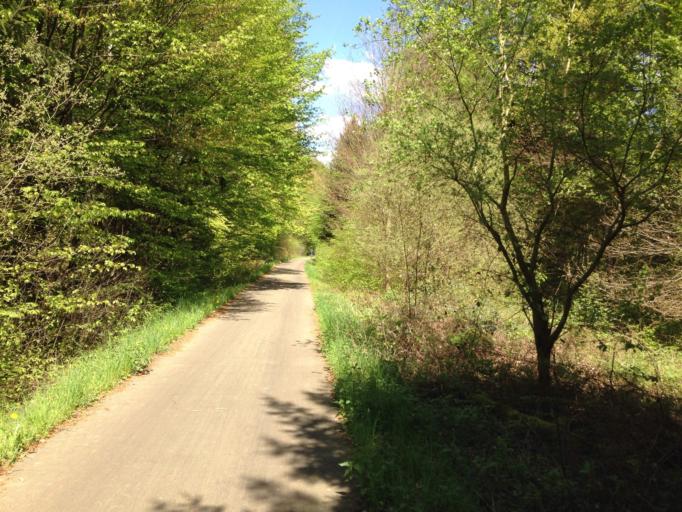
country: DE
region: Hesse
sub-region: Regierungsbezirk Giessen
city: Hungen
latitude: 50.4990
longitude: 8.9086
